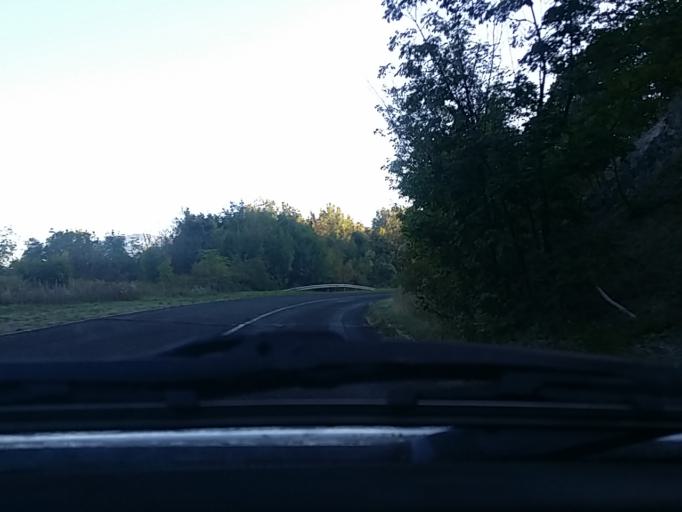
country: HU
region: Pest
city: Visegrad
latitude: 47.7274
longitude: 18.9677
